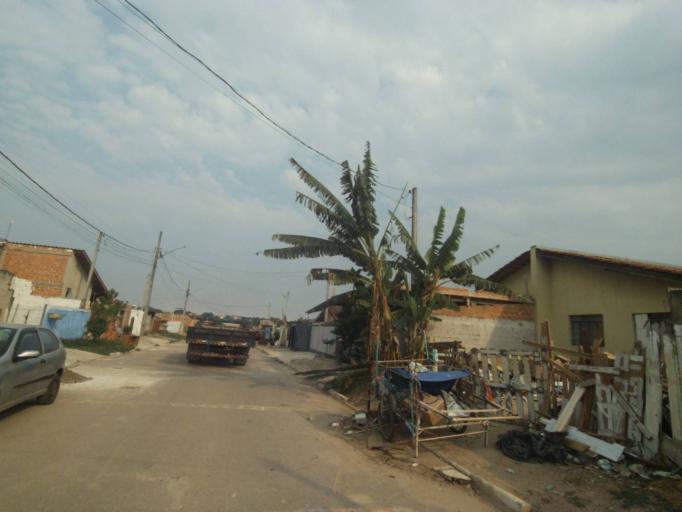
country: BR
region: Parana
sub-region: Sao Jose Dos Pinhais
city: Sao Jose dos Pinhais
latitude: -25.5327
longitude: -49.2302
